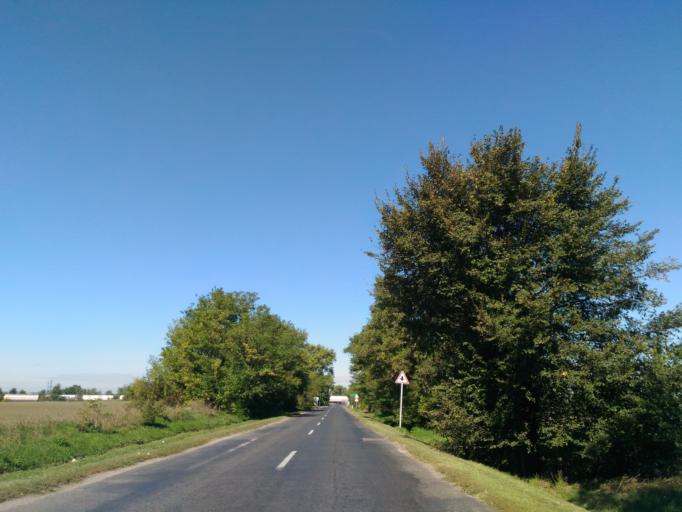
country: HU
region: Fejer
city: Ivancsa
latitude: 47.1738
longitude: 18.8131
